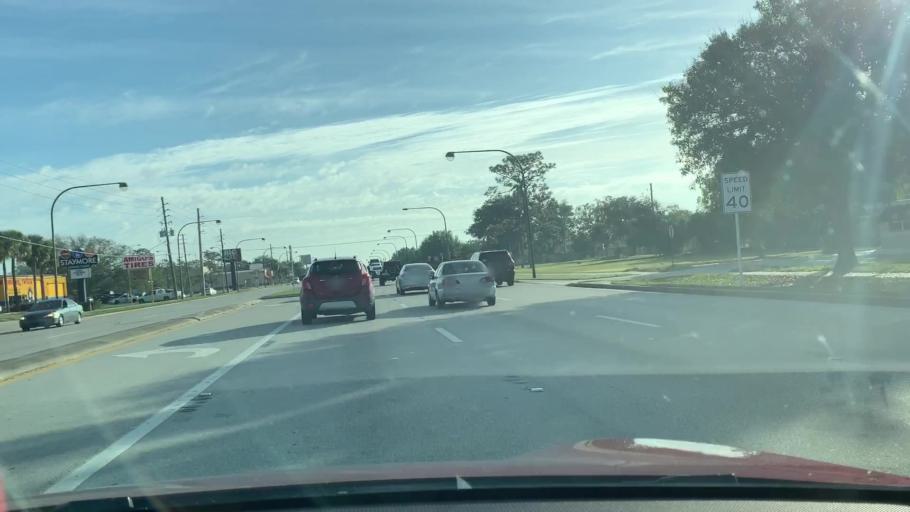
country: US
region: Florida
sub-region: Osceola County
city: Kissimmee
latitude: 28.3045
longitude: -81.4298
